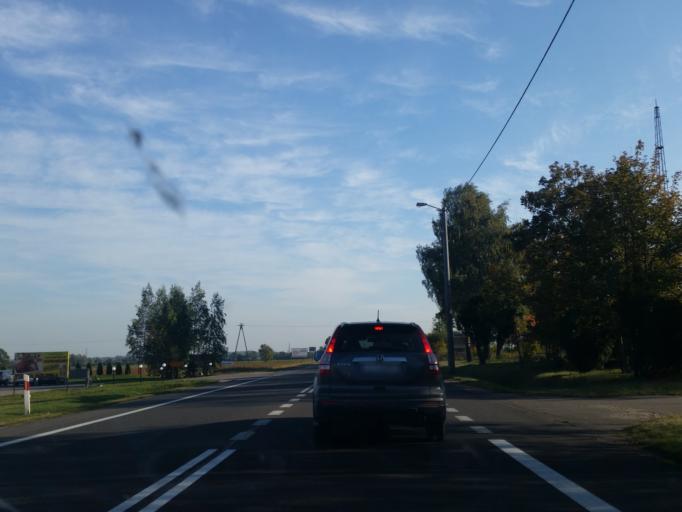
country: PL
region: Masovian Voivodeship
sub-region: Powiat plocki
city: Drobin
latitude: 52.7331
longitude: 20.0006
